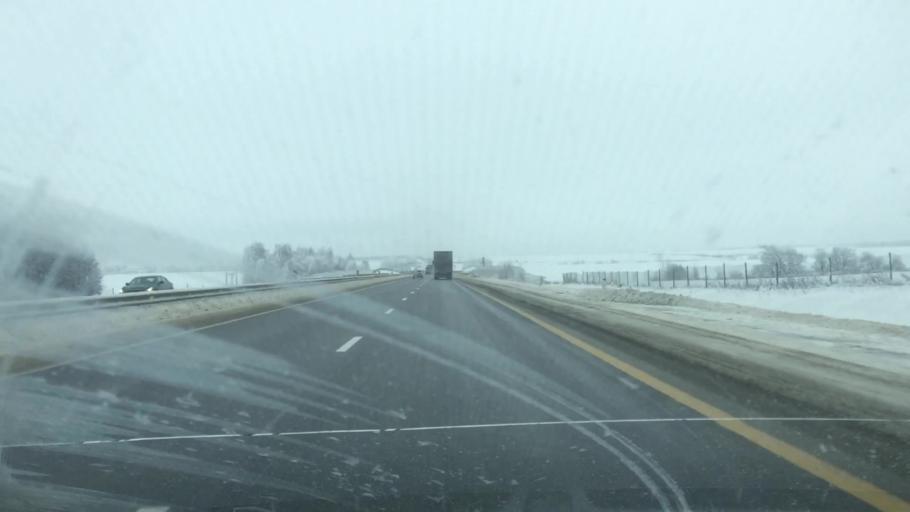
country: RU
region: Tula
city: Kazachka
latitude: 53.3407
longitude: 38.1811
